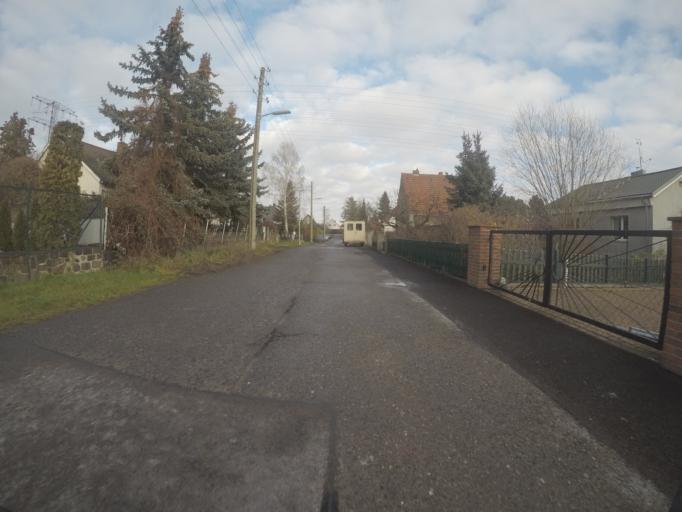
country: DE
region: Berlin
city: Falkenberg
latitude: 52.5890
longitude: 13.5379
